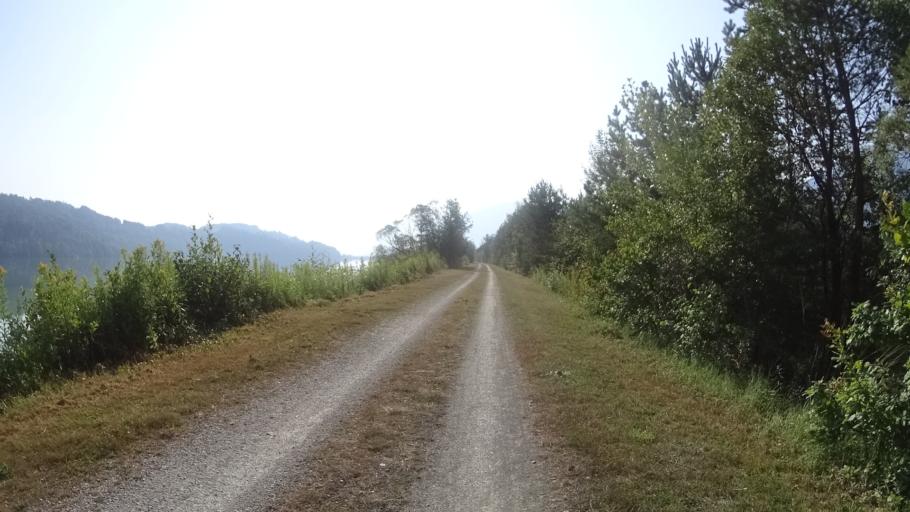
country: AT
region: Carinthia
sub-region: Politischer Bezirk Klagenfurt Land
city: Kottmannsdorf
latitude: 46.5441
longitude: 14.2268
